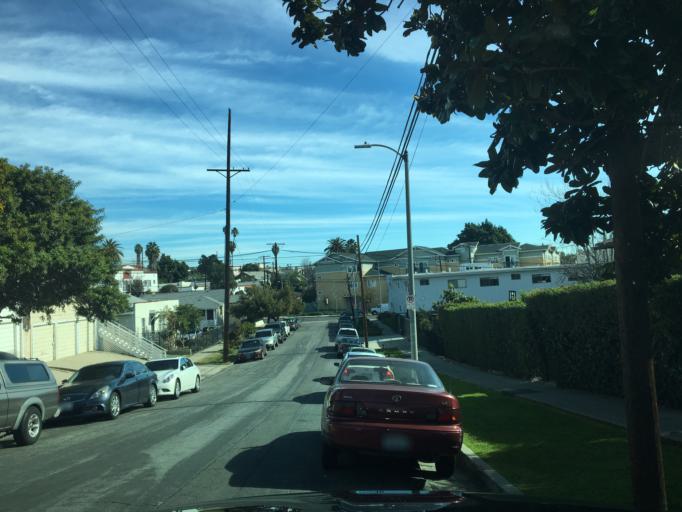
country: US
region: California
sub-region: Los Angeles County
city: Silver Lake
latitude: 34.0794
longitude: -118.2855
